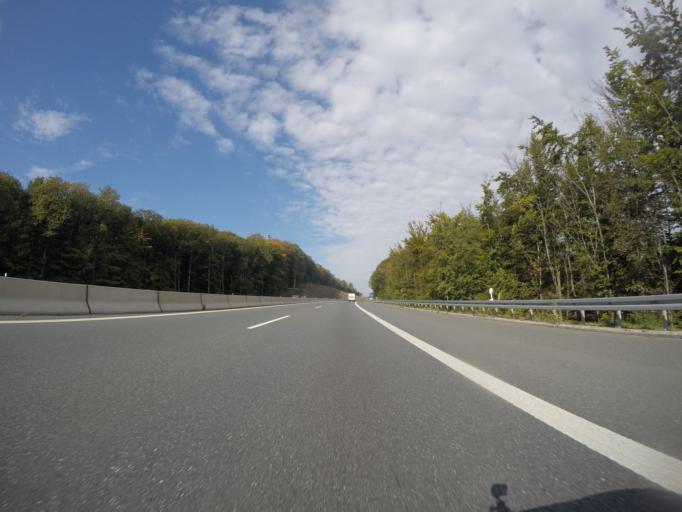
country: DE
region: Bavaria
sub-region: Regierungsbezirk Unterfranken
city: Schollbrunn
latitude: 49.8710
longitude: 9.4506
